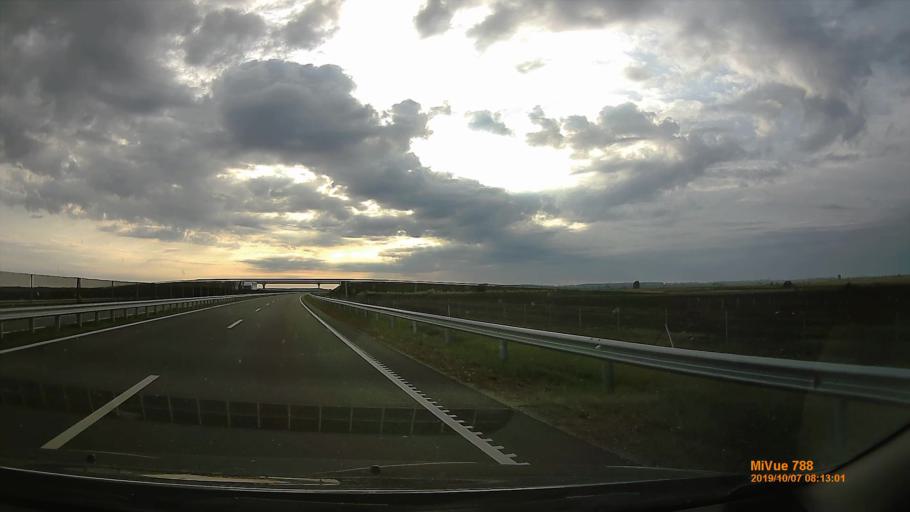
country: HU
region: Jasz-Nagykun-Szolnok
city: Cserkeszolo
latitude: 46.8820
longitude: 20.2358
